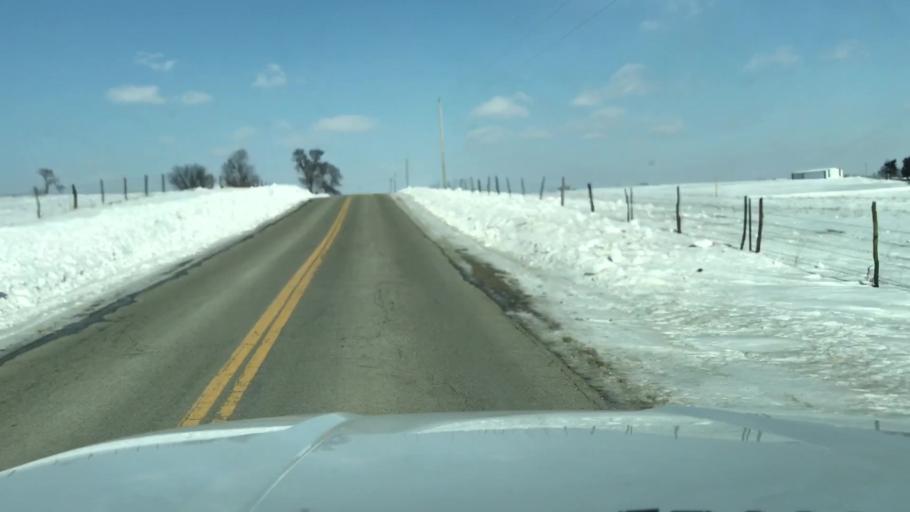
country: US
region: Missouri
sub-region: Nodaway County
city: Maryville
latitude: 40.3840
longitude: -94.7215
